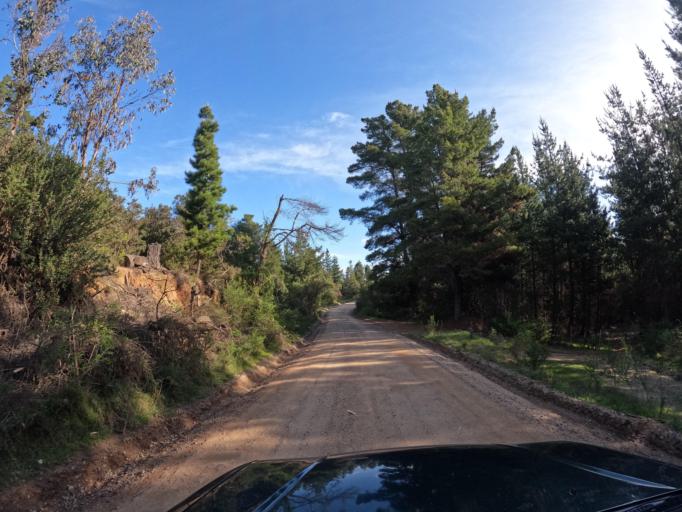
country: CL
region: Biobio
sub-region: Provincia de Biobio
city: La Laja
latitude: -37.1572
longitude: -72.7273
